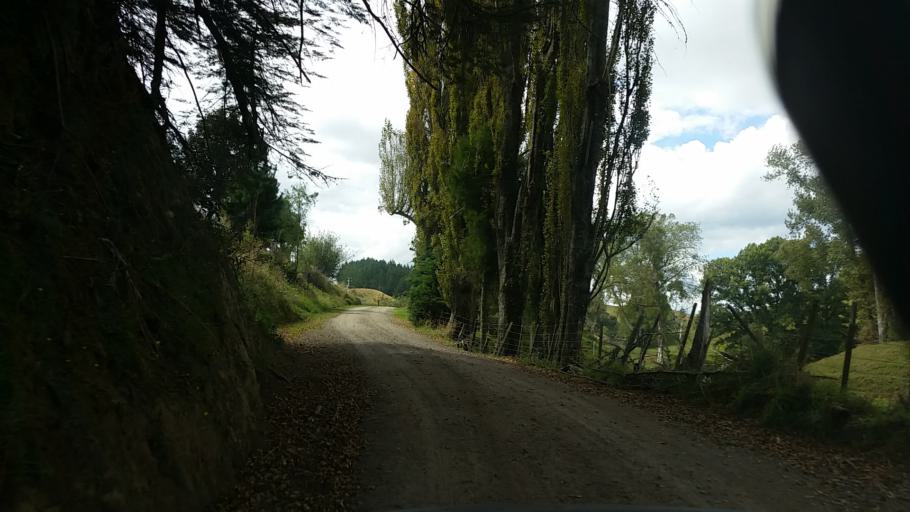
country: NZ
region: Taranaki
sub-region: South Taranaki District
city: Eltham
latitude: -39.2587
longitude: 174.5591
